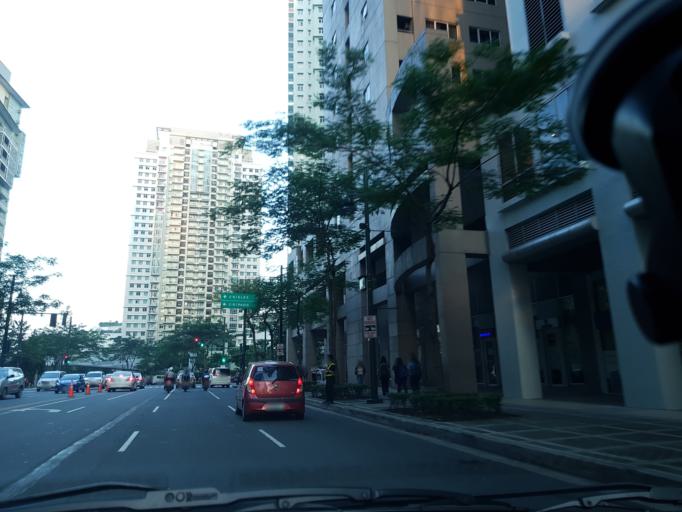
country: PH
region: Metro Manila
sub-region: Makati City
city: Makati City
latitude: 14.5475
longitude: 121.0516
